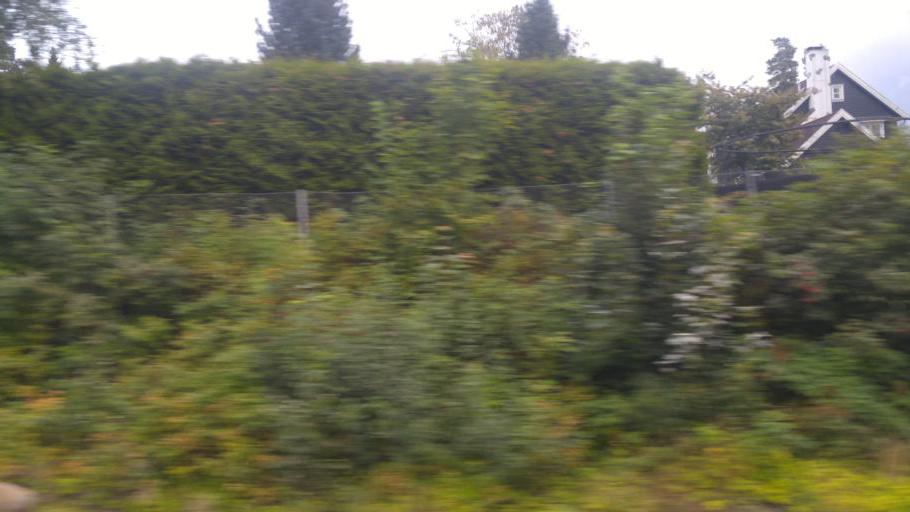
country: NO
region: Oslo
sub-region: Oslo
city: Sjolyststranda
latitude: 59.9565
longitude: 10.6957
